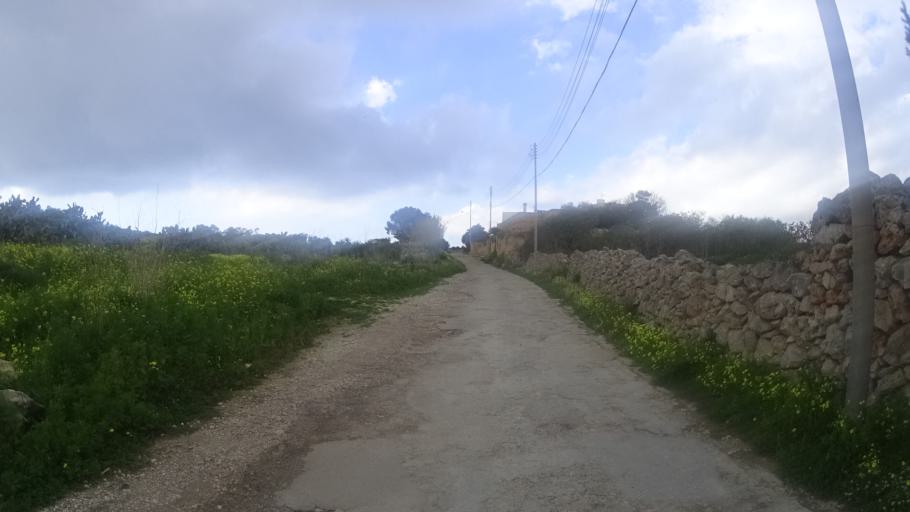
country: MT
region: L-Imgarr
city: Imgarr
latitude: 35.8956
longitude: 14.3685
